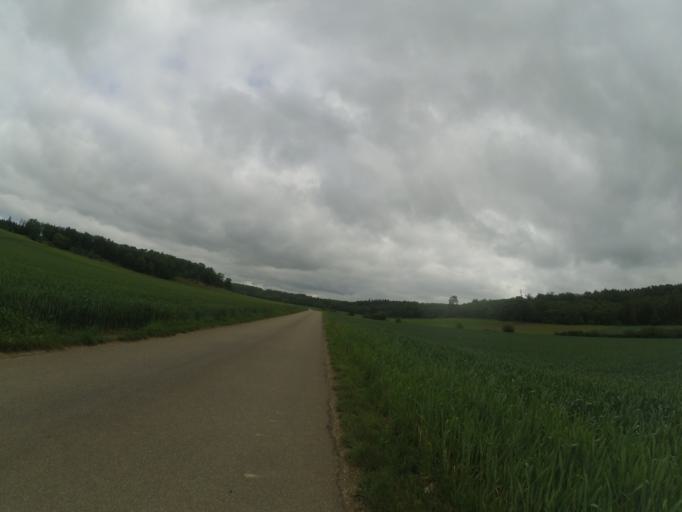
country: DE
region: Baden-Wuerttemberg
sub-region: Tuebingen Region
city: Bernstadt
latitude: 48.5096
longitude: 10.0302
